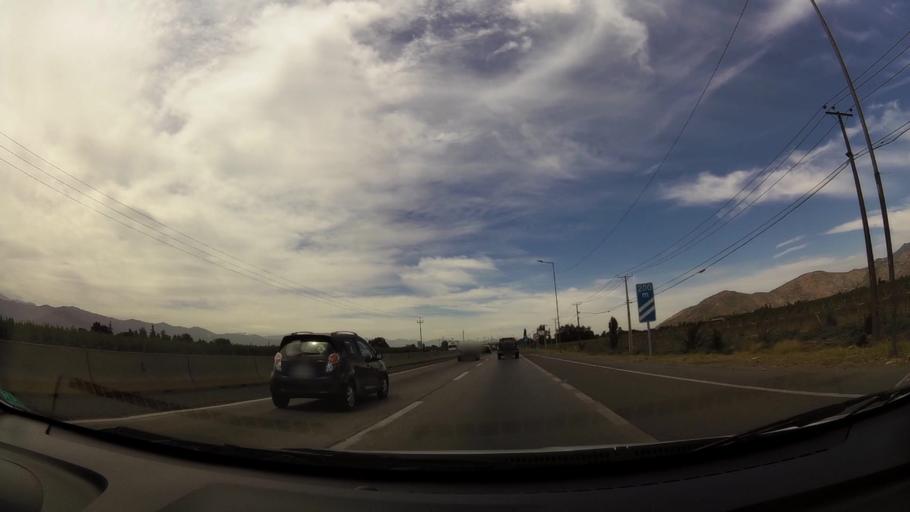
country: CL
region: O'Higgins
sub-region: Provincia de Cachapoal
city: Graneros
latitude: -33.9958
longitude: -70.7007
